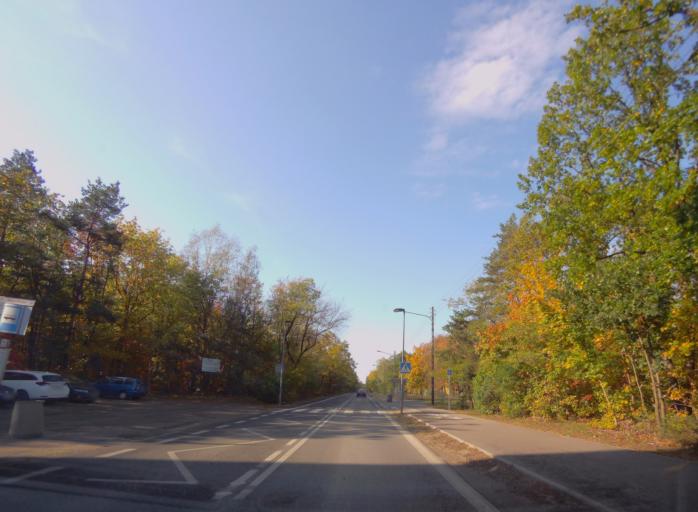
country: PL
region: Masovian Voivodeship
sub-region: Warszawa
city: Wawer
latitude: 52.1587
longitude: 21.1982
